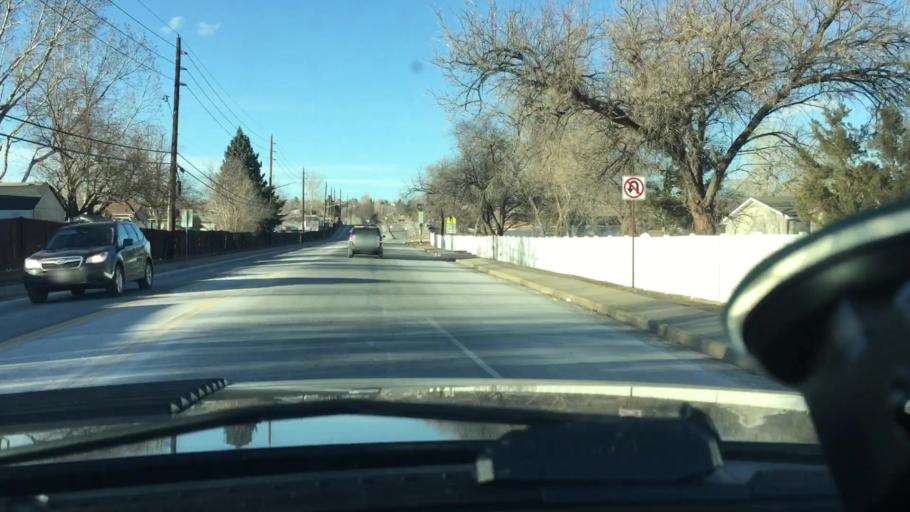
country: US
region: Colorado
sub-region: Adams County
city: Federal Heights
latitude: 39.8660
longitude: -105.0061
